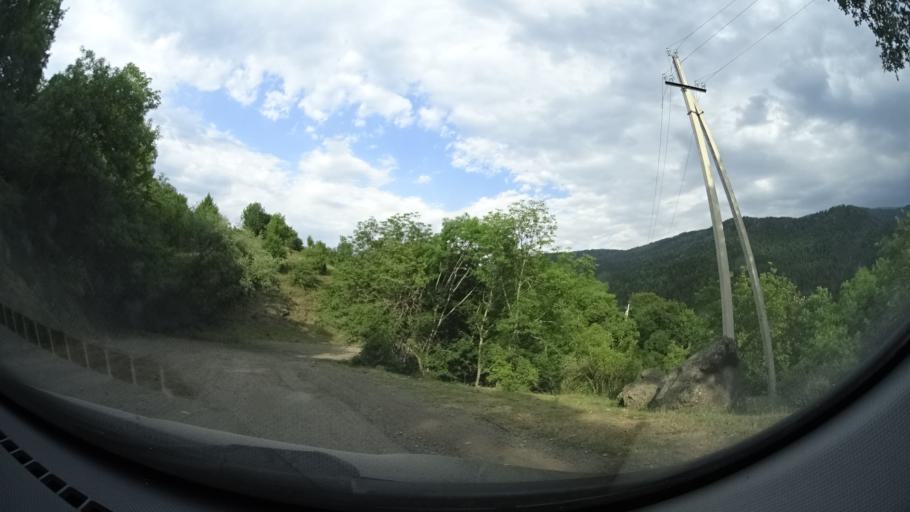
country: GE
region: Samtskhe-Javakheti
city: Adigeni
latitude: 41.6676
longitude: 42.6272
